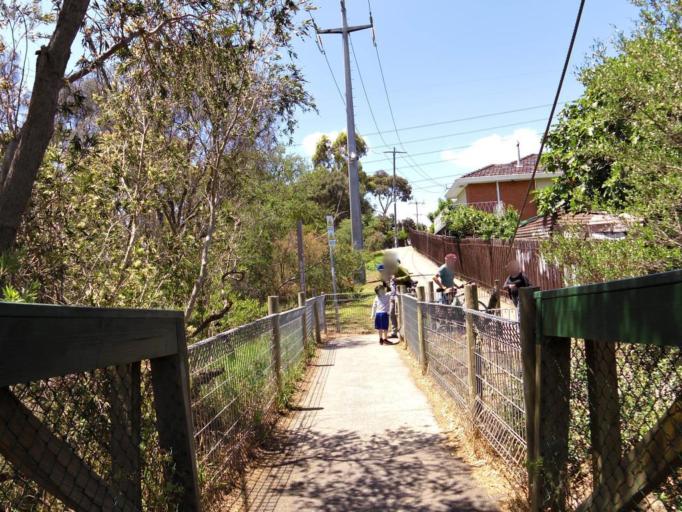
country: AU
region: Victoria
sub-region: Moreland
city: Coburg
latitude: -37.7465
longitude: 144.9805
